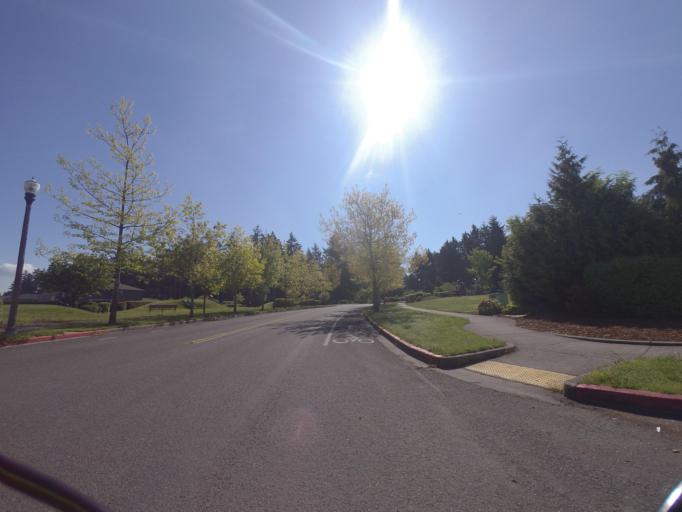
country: US
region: Washington
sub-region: Pierce County
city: Waller
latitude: 47.2136
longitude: -122.4067
